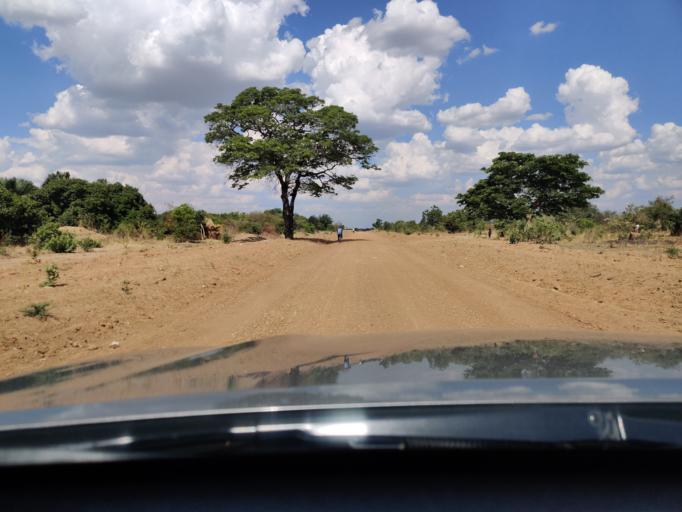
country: ZM
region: Central
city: Chibombo
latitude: -14.7592
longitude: 27.8718
